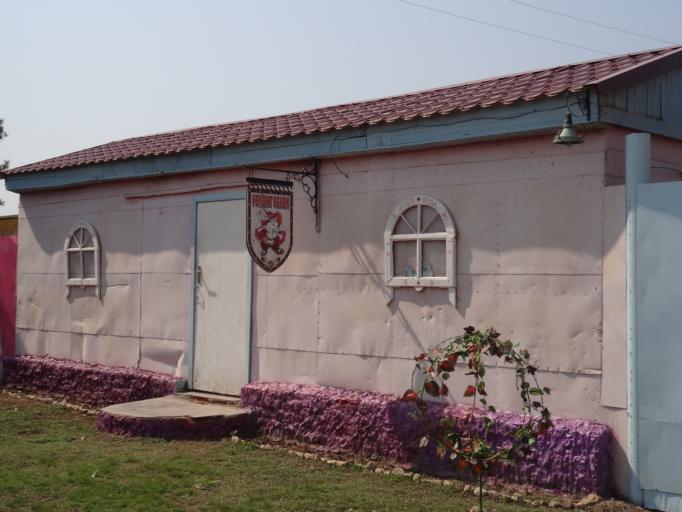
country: RU
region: Saratov
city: Privolzhskiy
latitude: 51.2514
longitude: 45.9107
